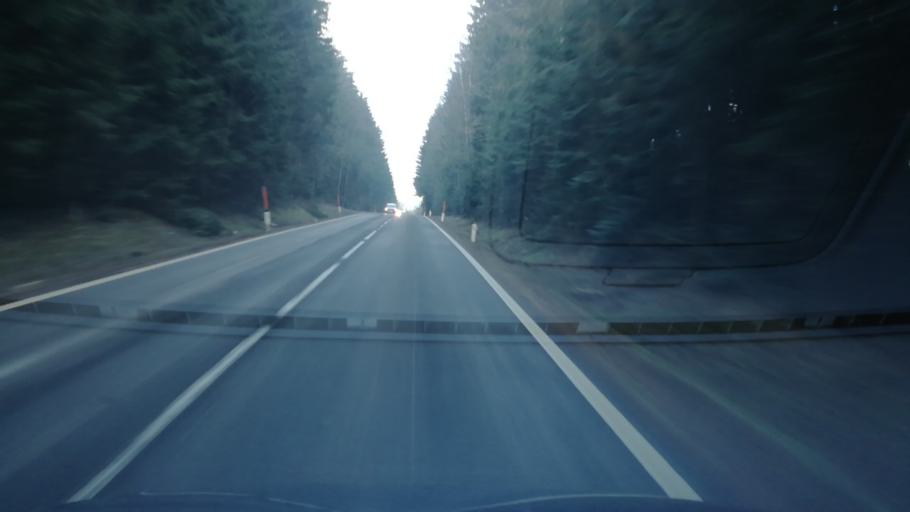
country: AT
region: Upper Austria
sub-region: Politischer Bezirk Ried im Innkreis
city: Waldzell
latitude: 48.1852
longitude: 13.4399
